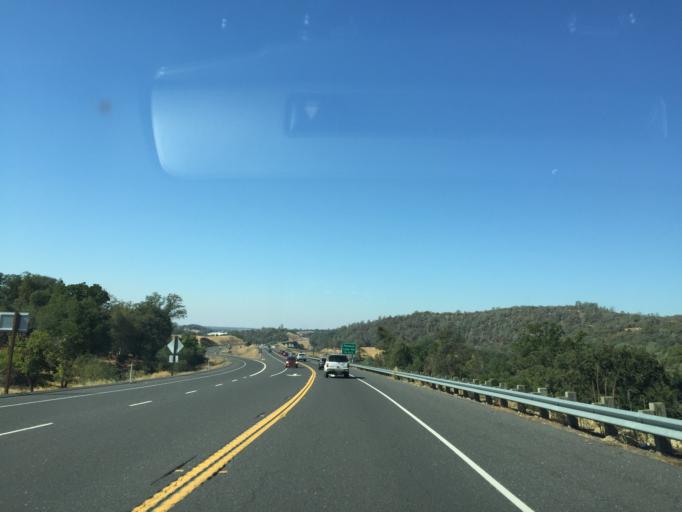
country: US
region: California
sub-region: Tuolumne County
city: East Sonora
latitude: 37.9813
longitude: -120.3307
